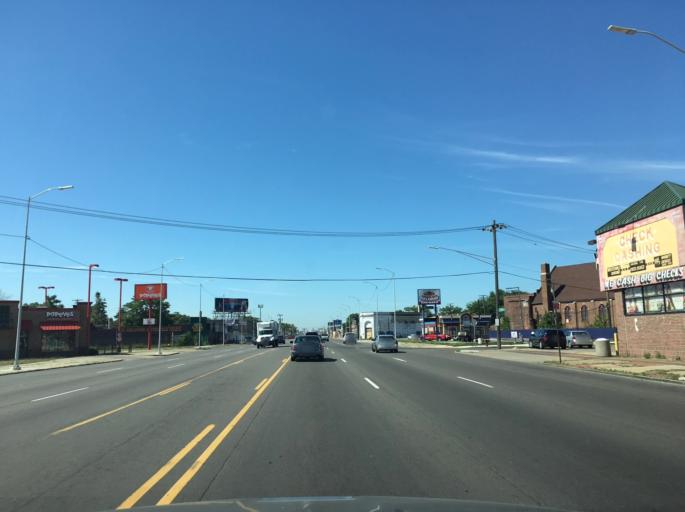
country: US
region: Michigan
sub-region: Macomb County
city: Eastpointe
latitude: 42.4346
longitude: -82.9781
